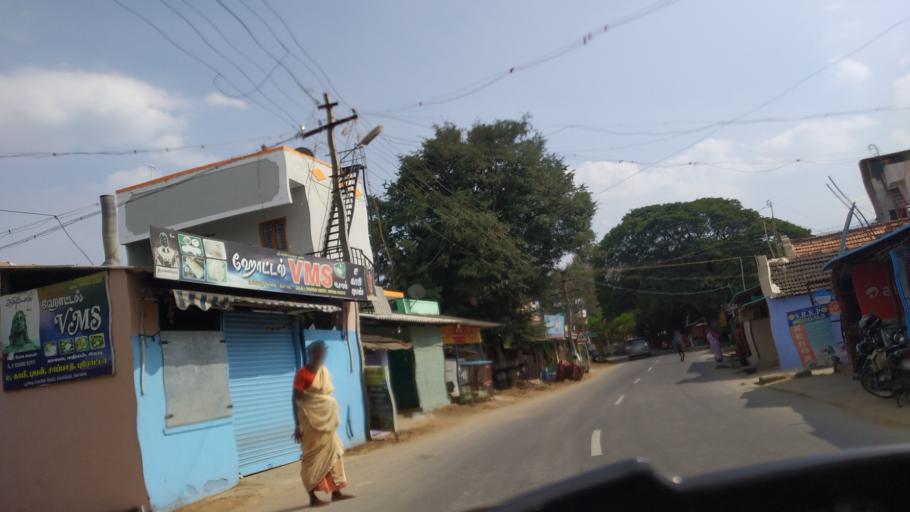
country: IN
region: Tamil Nadu
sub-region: Coimbatore
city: Perur
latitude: 10.9568
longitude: 76.7598
